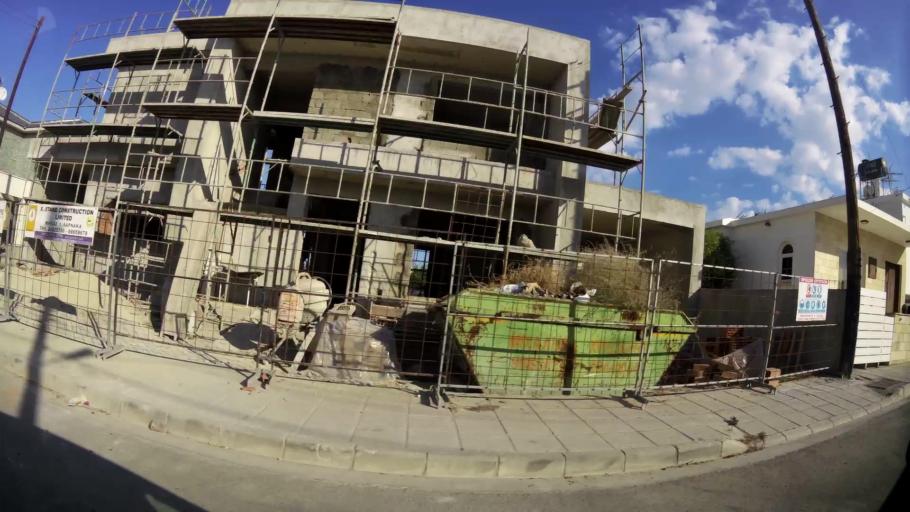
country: CY
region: Larnaka
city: Aradippou
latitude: 34.9477
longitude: 33.5977
